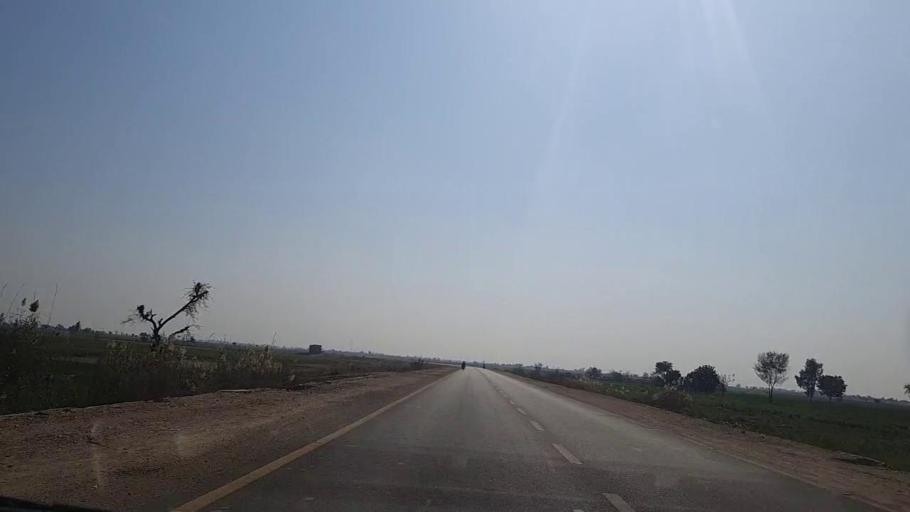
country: PK
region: Sindh
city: Sakrand
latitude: 26.0898
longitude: 68.4016
